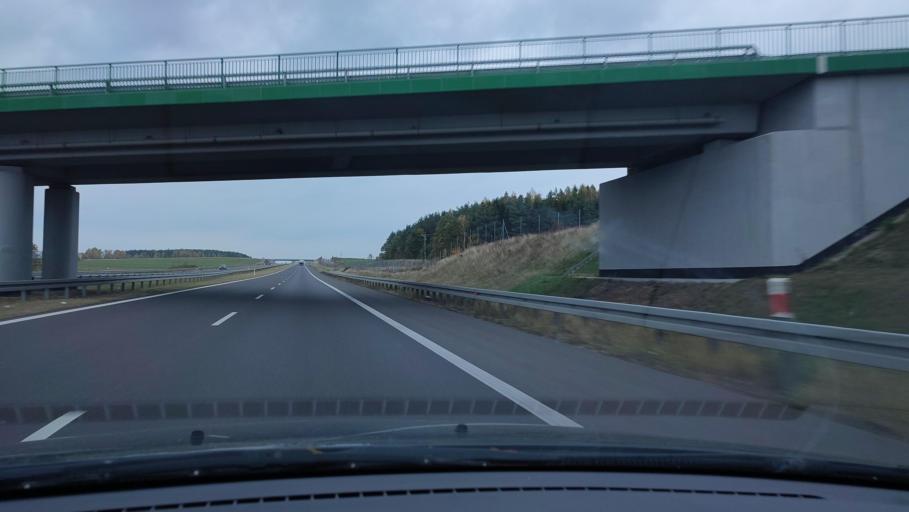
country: PL
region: Warmian-Masurian Voivodeship
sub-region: Powiat nidzicki
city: Nidzica
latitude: 53.3122
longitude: 20.4378
